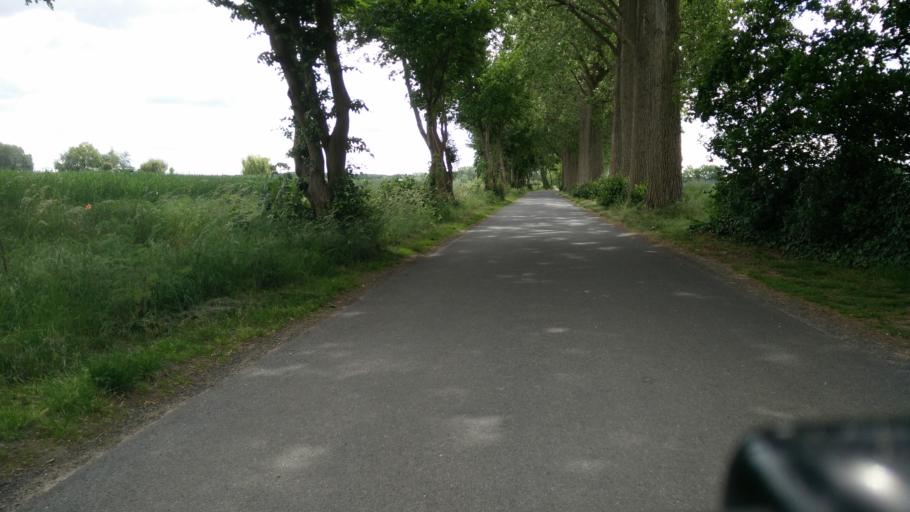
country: DE
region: Lower Saxony
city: Hagenburg
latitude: 52.4501
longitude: 9.3649
